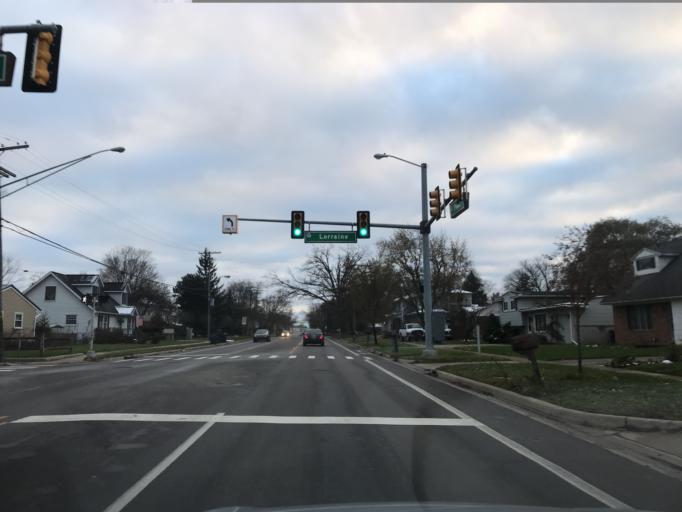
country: US
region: Michigan
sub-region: Washtenaw County
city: Ann Arbor
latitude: 42.2386
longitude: -83.7001
